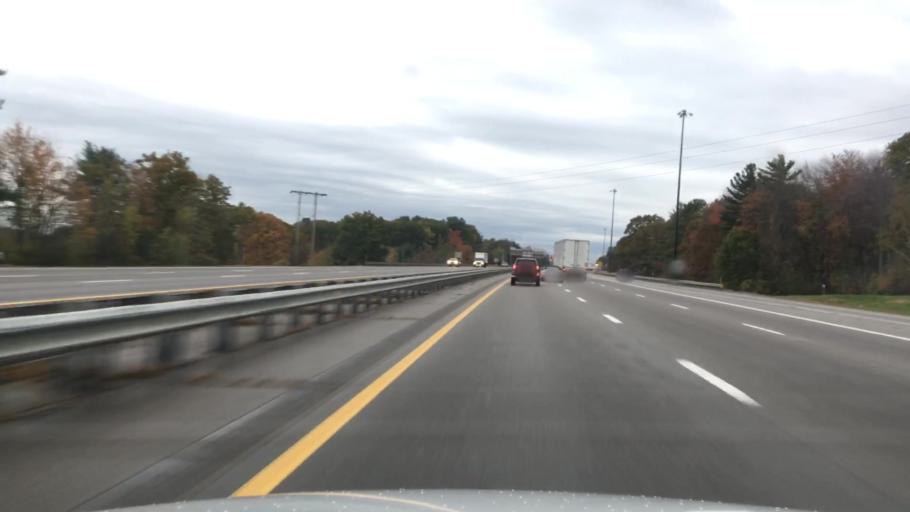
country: US
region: Maine
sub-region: York County
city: Kittery
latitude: 43.1015
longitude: -70.7518
